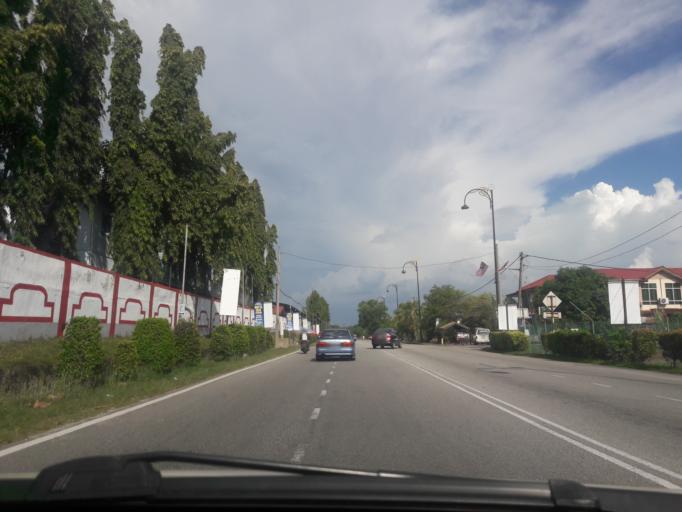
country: MY
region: Kedah
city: Sungai Petani
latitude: 5.6526
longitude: 100.5009
